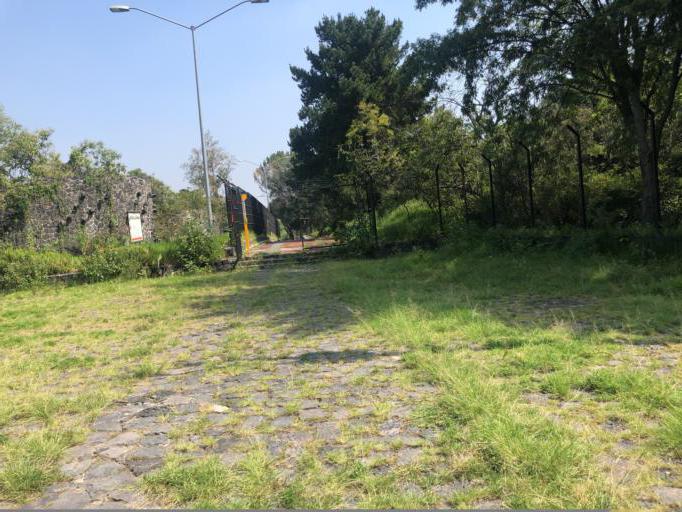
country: MX
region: Mexico City
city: Tlalpan
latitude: 19.3151
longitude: -99.1823
